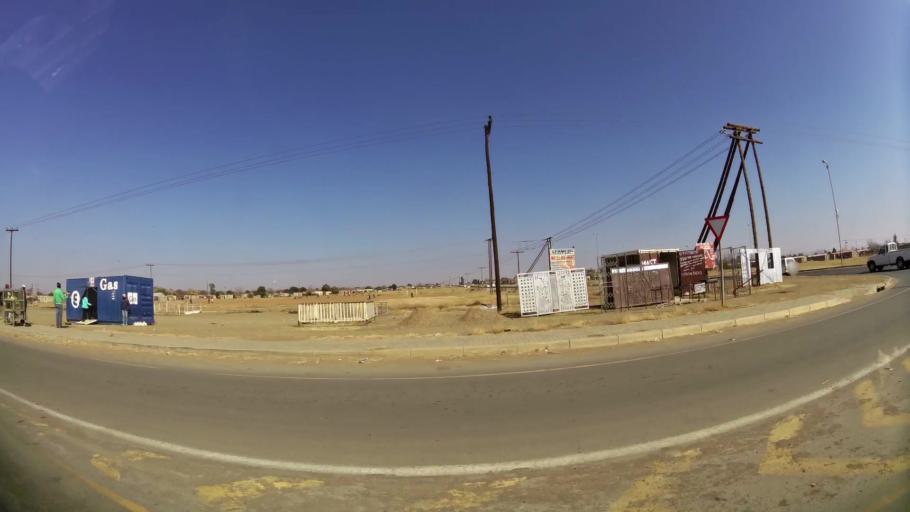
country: ZA
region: Orange Free State
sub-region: Mangaung Metropolitan Municipality
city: Bloemfontein
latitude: -29.1618
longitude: 26.2567
